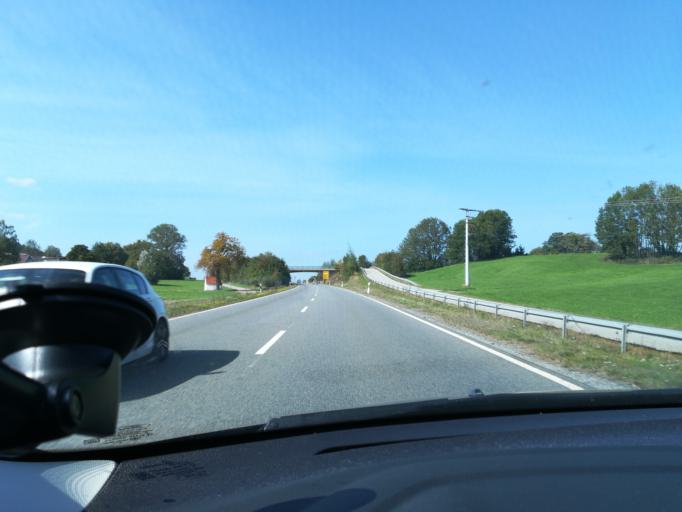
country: DE
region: Bavaria
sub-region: Upper Bavaria
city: Ebersberg
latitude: 48.0646
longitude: 11.9375
